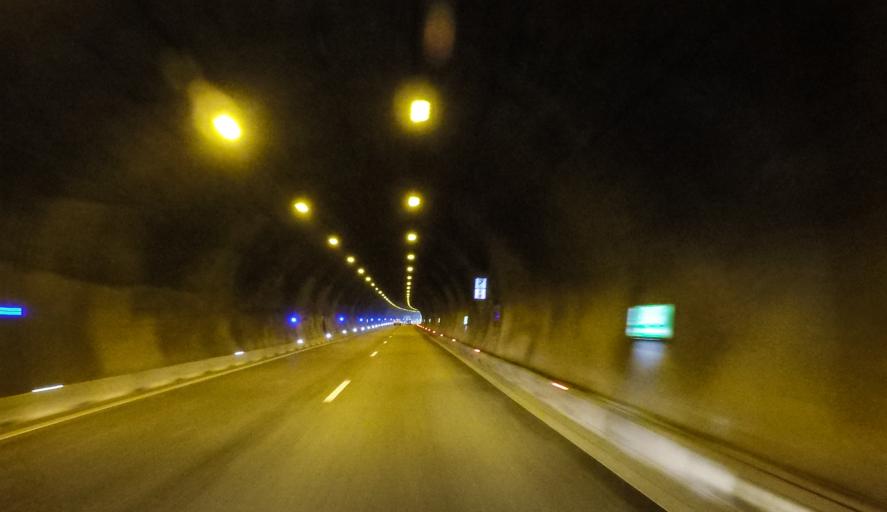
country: GE
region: Shida Kartli
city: Gori
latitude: 42.0114
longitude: 44.0495
